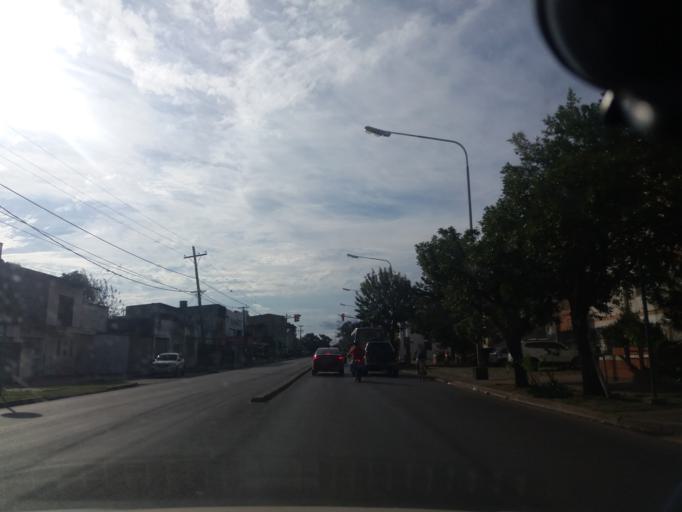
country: AR
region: Corrientes
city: Corrientes
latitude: -27.4869
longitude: -58.8227
